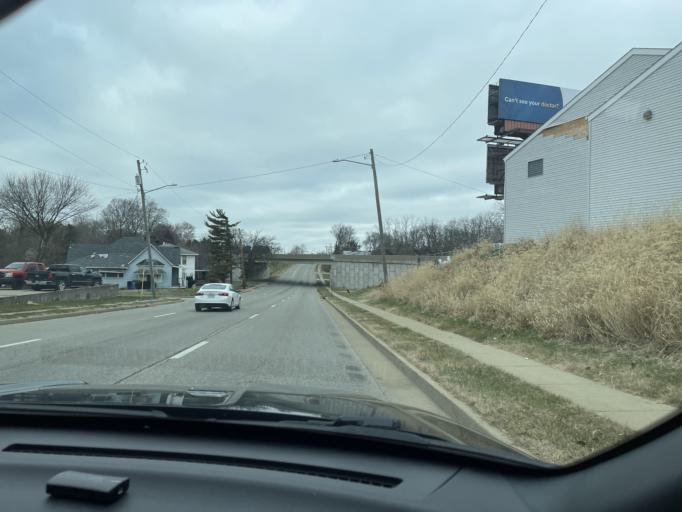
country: US
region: Illinois
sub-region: Sangamon County
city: Leland Grove
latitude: 39.8059
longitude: -89.6736
